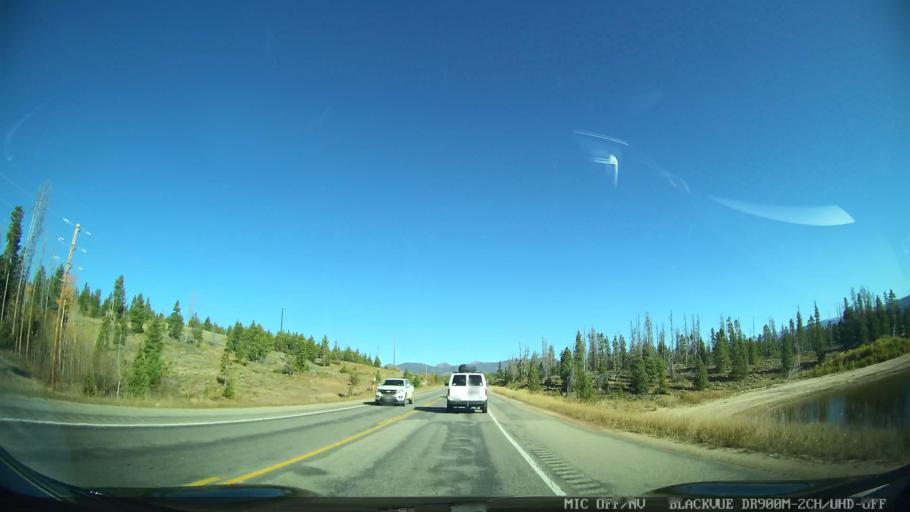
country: US
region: Colorado
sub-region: Grand County
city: Granby
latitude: 40.1674
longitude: -105.8992
